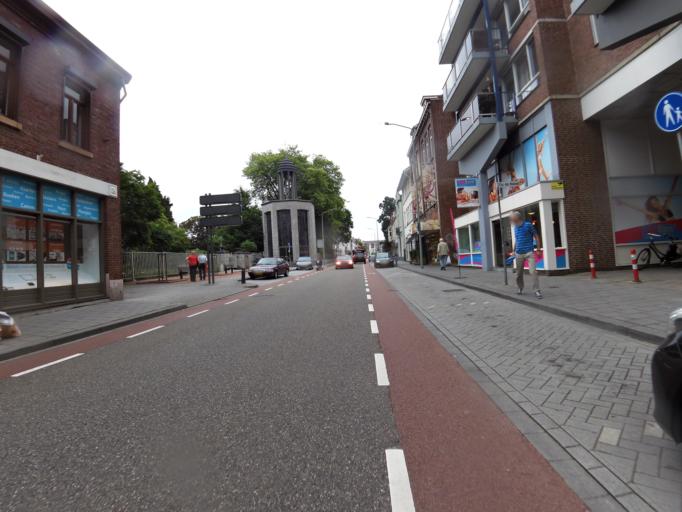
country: NL
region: Limburg
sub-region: Gemeente Heerlen
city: Heerlen
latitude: 50.8850
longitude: 5.9814
